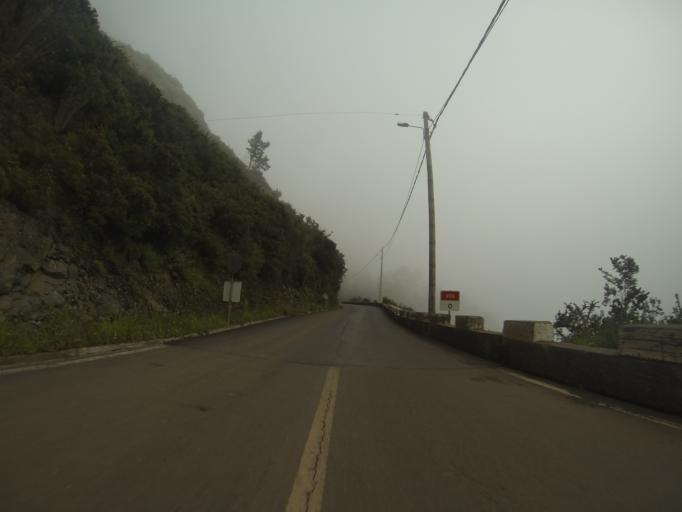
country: PT
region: Madeira
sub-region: Camara de Lobos
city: Curral das Freiras
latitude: 32.7006
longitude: -16.9529
